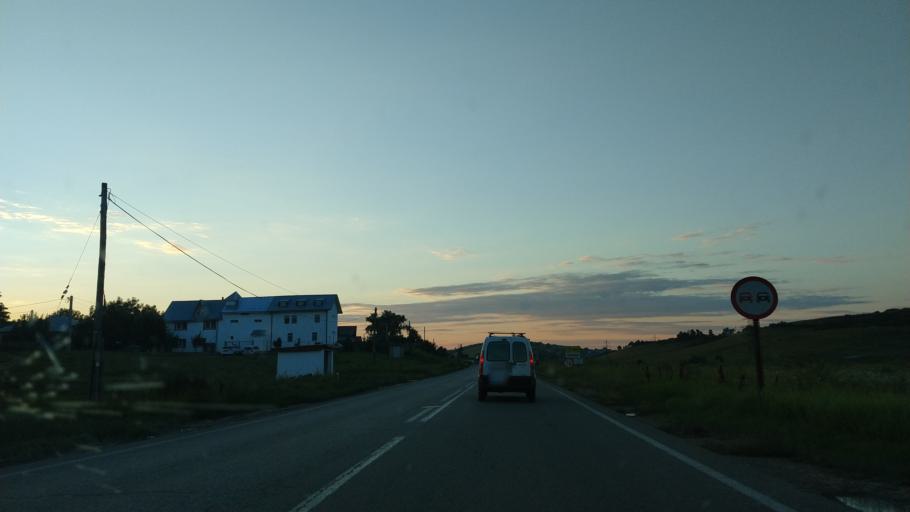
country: RO
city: Vanatori
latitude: 47.2294
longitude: 27.5373
